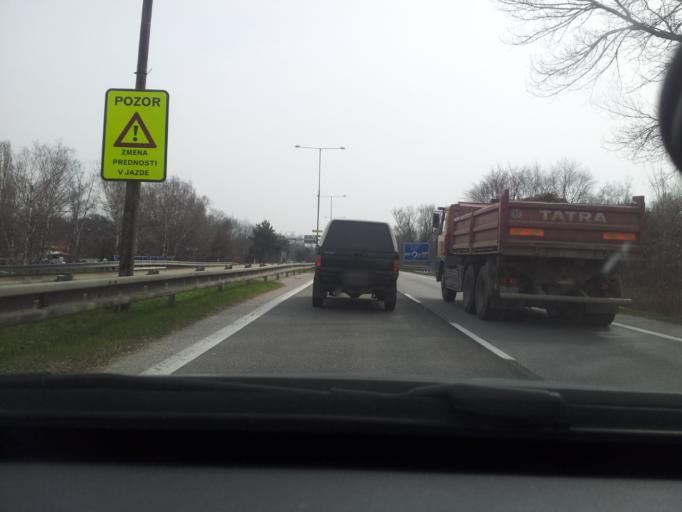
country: SK
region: Nitriansky
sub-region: Okres Nitra
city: Nitra
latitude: 48.3214
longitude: 18.0932
